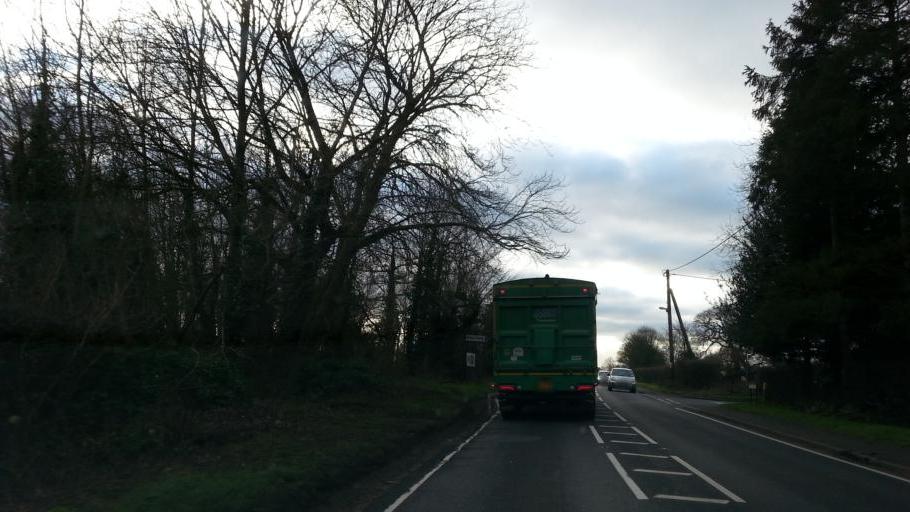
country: GB
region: England
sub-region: Suffolk
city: Great Barton
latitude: 52.2639
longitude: 0.7639
